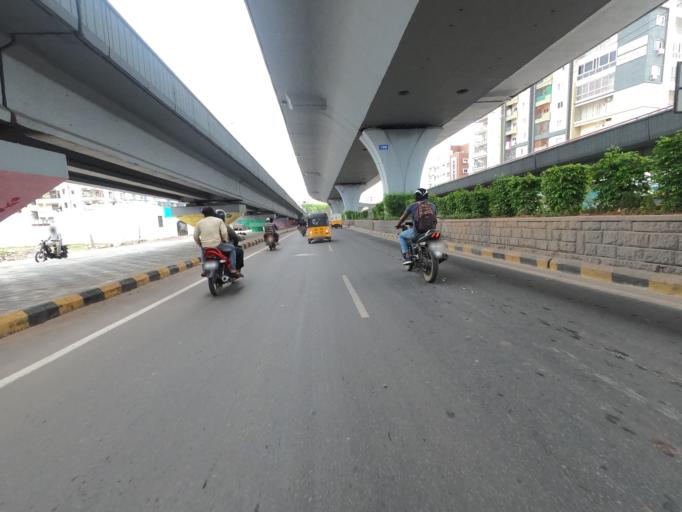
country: IN
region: Telangana
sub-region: Hyderabad
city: Hyderabad
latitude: 17.3501
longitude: 78.4171
